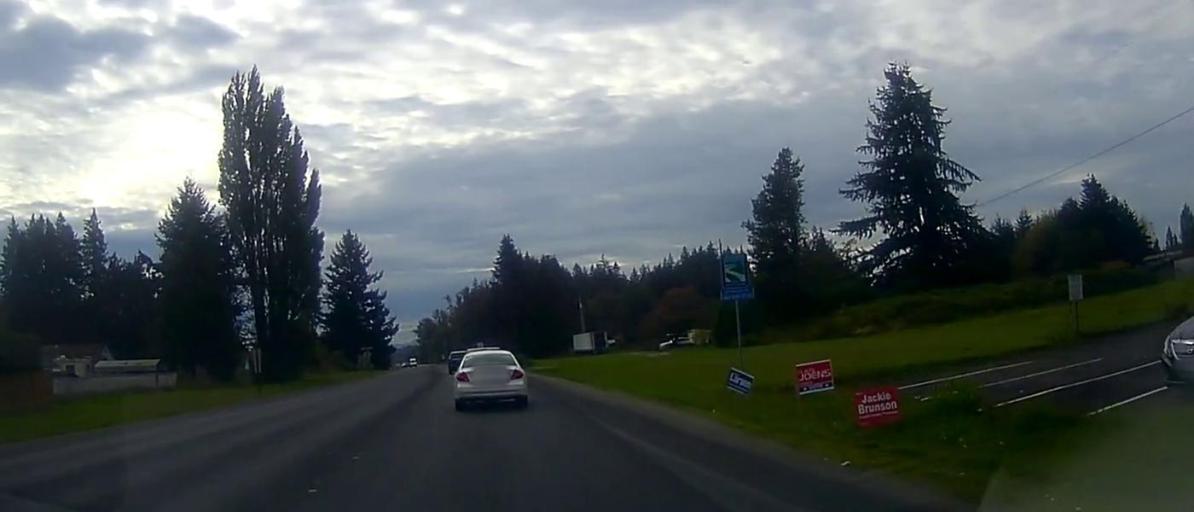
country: US
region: Washington
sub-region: Skagit County
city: Sedro-Woolley
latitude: 48.5028
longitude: -122.2471
